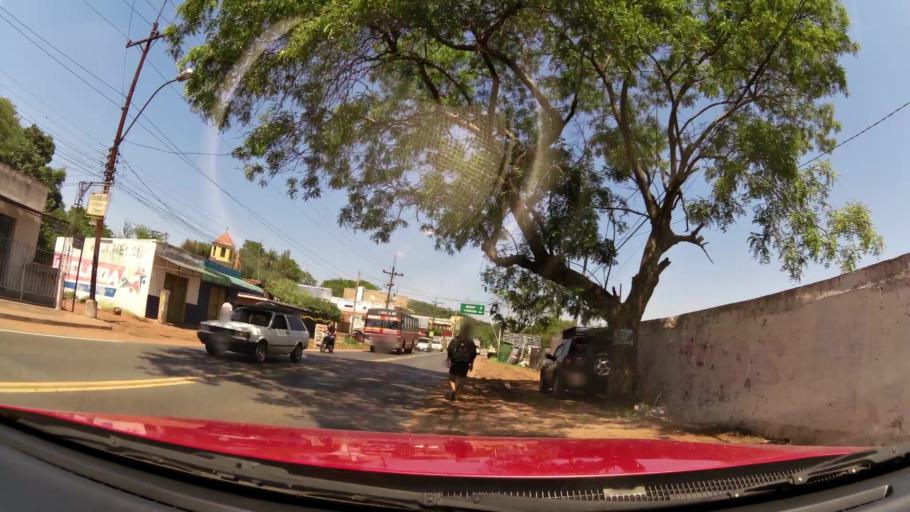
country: PY
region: Central
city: Nemby
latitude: -25.3962
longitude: -57.5298
